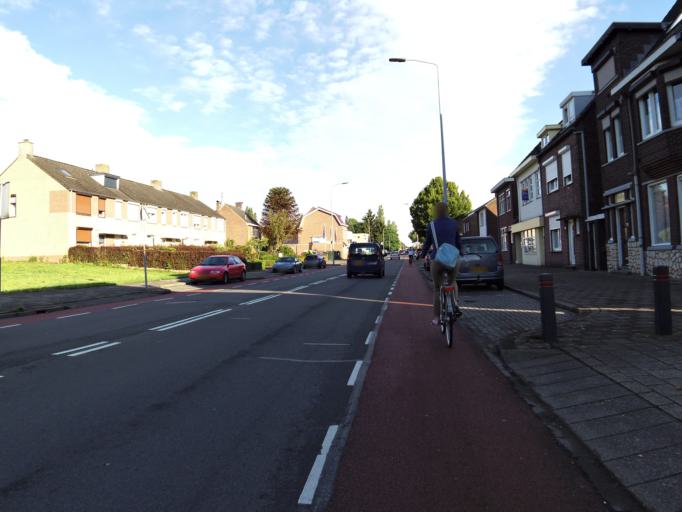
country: NL
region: Limburg
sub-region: Gemeente Heerlen
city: Heerlen
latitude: 50.8698
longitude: 5.9971
